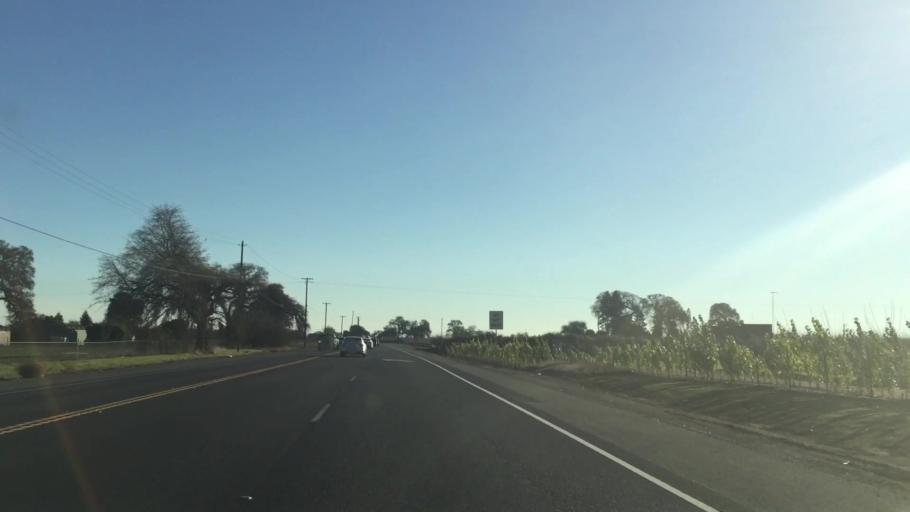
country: US
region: California
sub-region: Sutter County
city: Live Oak
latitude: 39.3480
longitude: -121.6010
